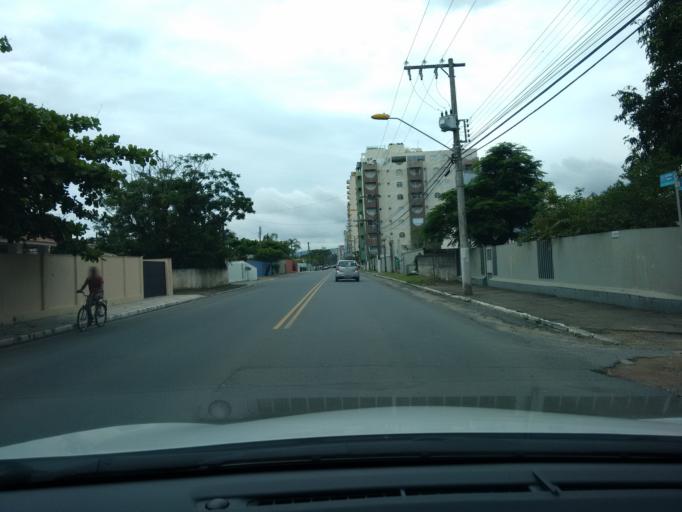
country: BR
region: Santa Catarina
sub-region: Penha
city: Penha
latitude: -26.7467
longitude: -48.6791
